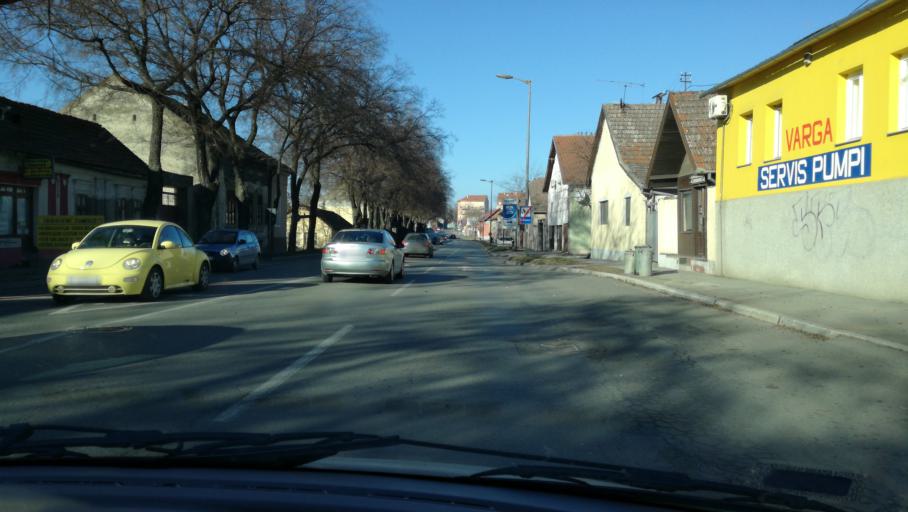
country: RS
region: Autonomna Pokrajina Vojvodina
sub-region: Severnobacki Okrug
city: Subotica
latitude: 46.0901
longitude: 19.6650
